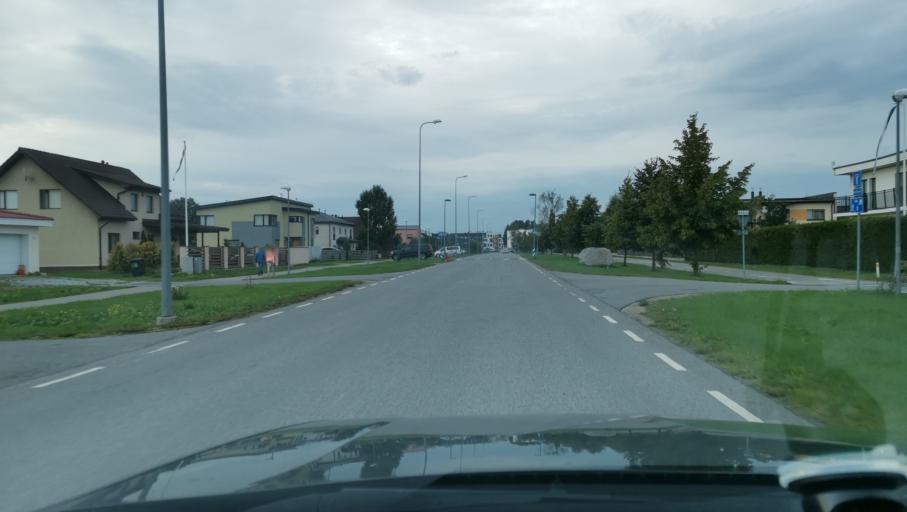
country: EE
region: Harju
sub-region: Saue vald
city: Laagri
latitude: 59.4253
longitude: 24.6223
